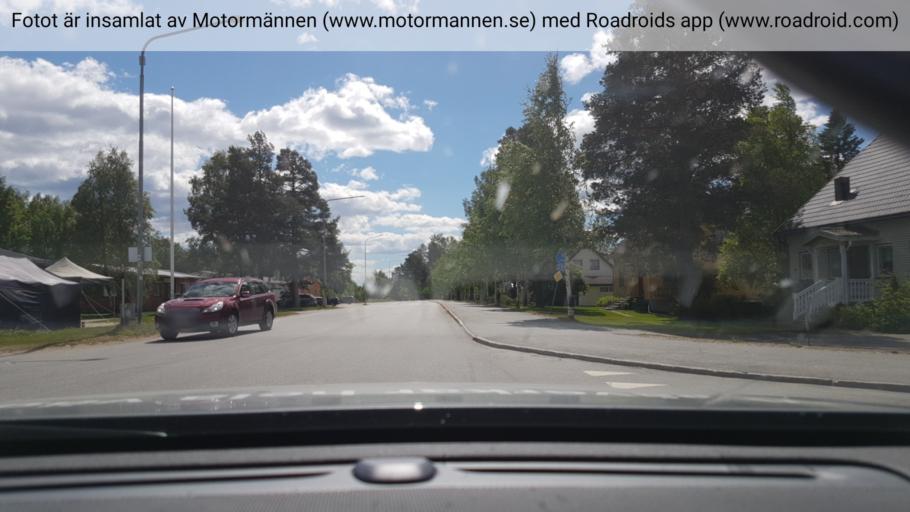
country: SE
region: Vaesterbotten
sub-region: Nordmalings Kommun
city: Nordmaling
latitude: 63.5778
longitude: 19.4871
